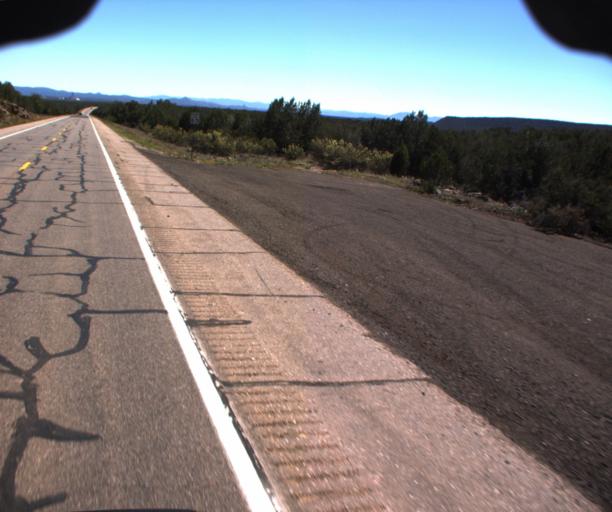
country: US
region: Arizona
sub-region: Yavapai County
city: Paulden
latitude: 35.0604
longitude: -112.3988
